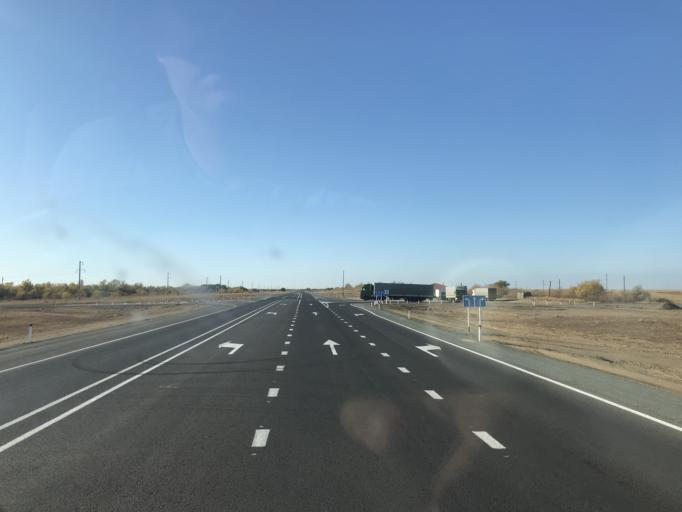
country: KZ
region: Pavlodar
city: Kurchatov
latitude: 51.4127
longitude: 78.2456
